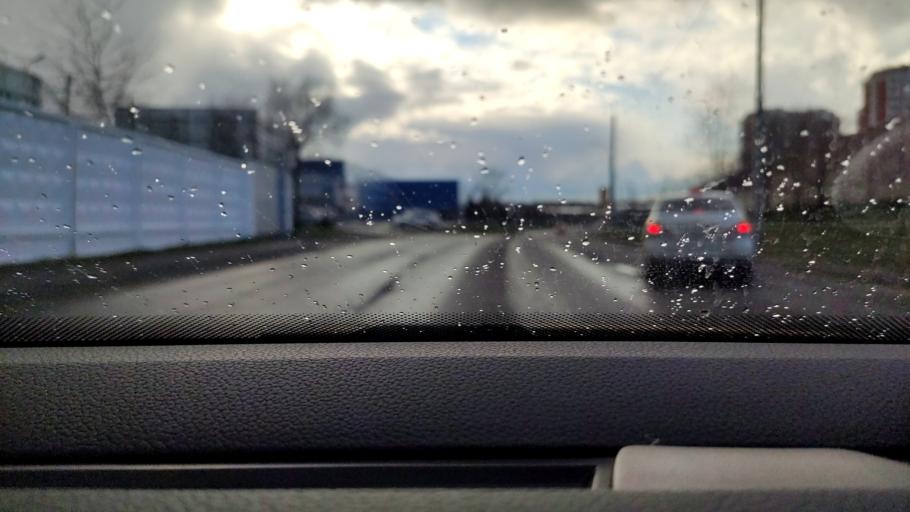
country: RU
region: Moskovskaya
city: Saltykovka
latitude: 55.7411
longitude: 37.9648
